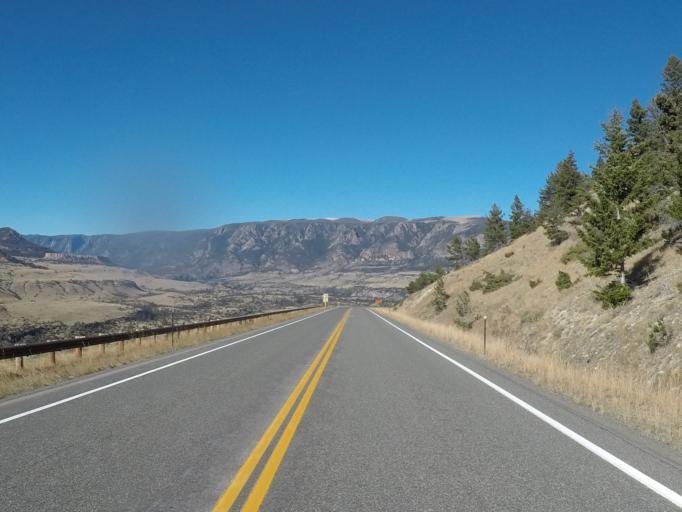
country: US
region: Wyoming
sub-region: Park County
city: Cody
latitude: 44.7543
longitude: -109.4030
